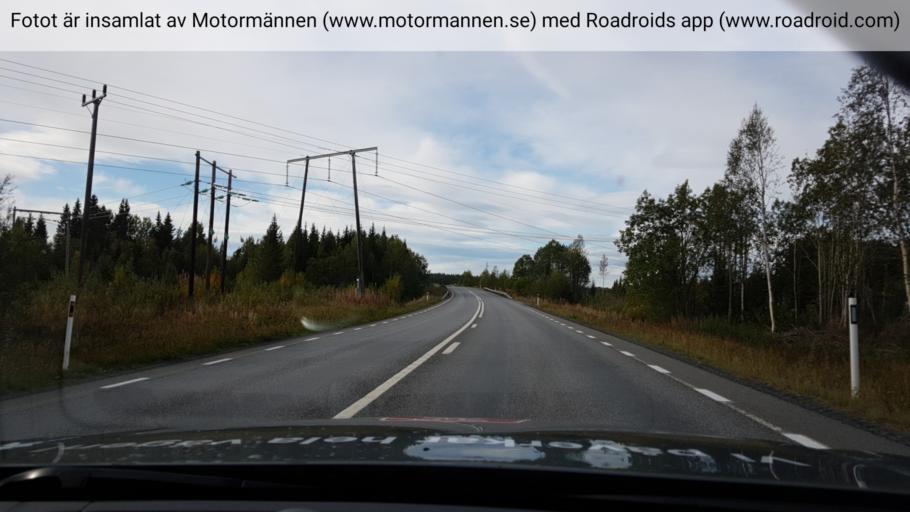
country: SE
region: Jaemtland
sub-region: Krokoms Kommun
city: Valla
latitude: 63.3357
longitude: 13.9796
